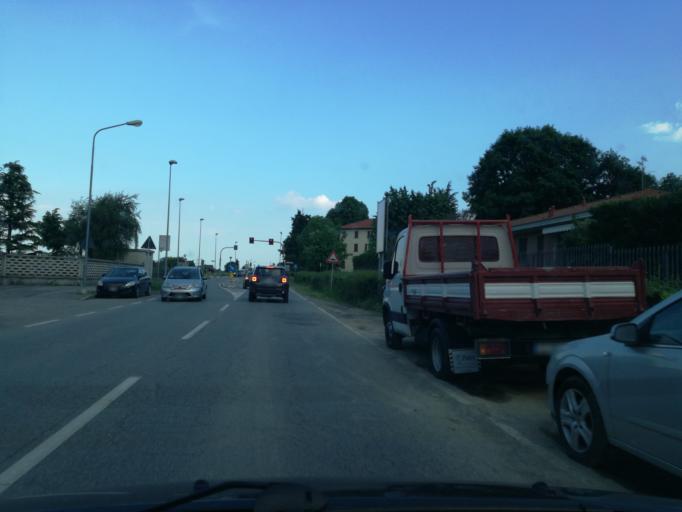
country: IT
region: Lombardy
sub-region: Provincia di Monza e Brianza
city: Cornate d'Adda
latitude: 45.6434
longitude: 9.4668
